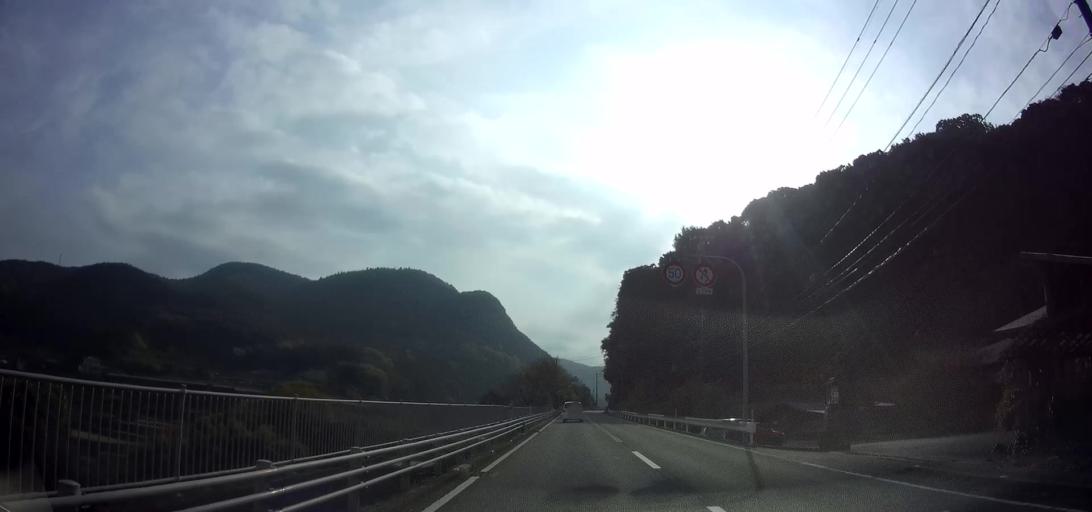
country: JP
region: Nagasaki
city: Shimabara
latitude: 32.7798
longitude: 130.2085
